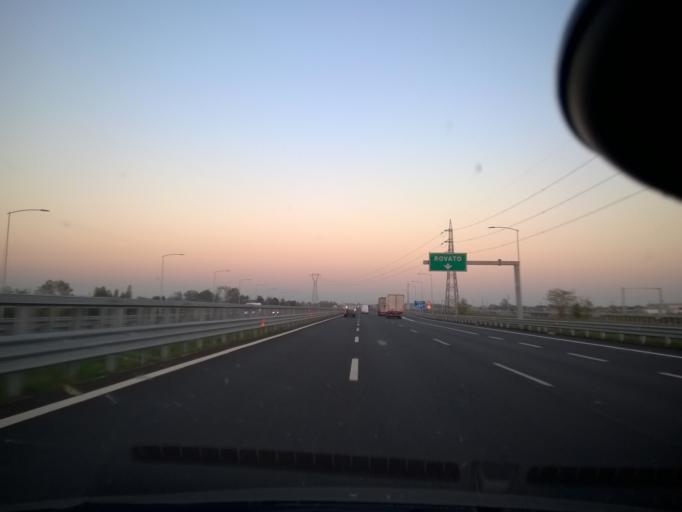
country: IT
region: Lombardy
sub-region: Provincia di Brescia
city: Duomo
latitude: 45.5235
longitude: 10.0051
